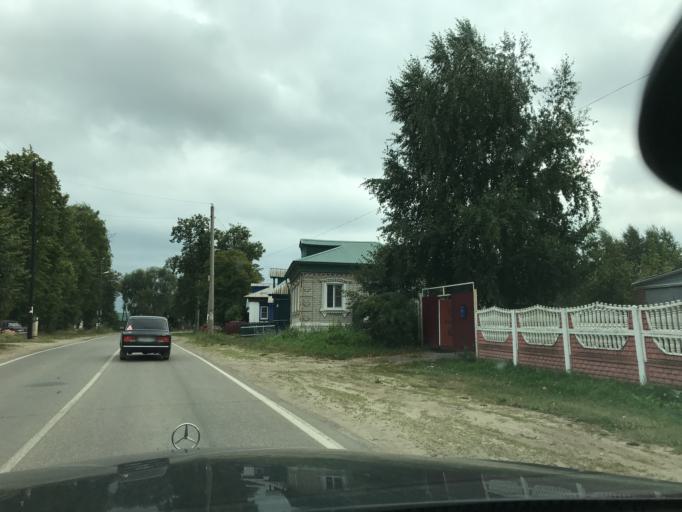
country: RU
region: Nizjnij Novgorod
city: Pavlovo
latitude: 55.9964
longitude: 43.0359
